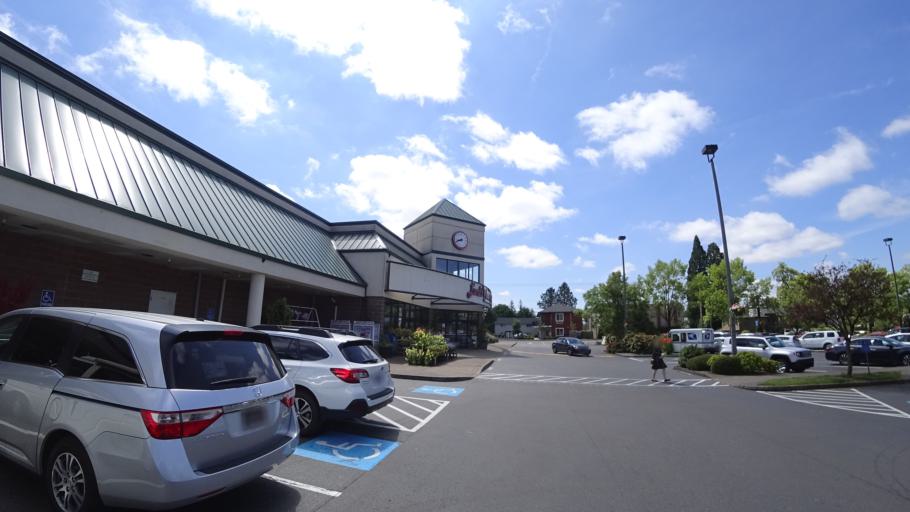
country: US
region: Oregon
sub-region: Washington County
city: Garden Home-Whitford
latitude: 45.4663
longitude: -122.7516
